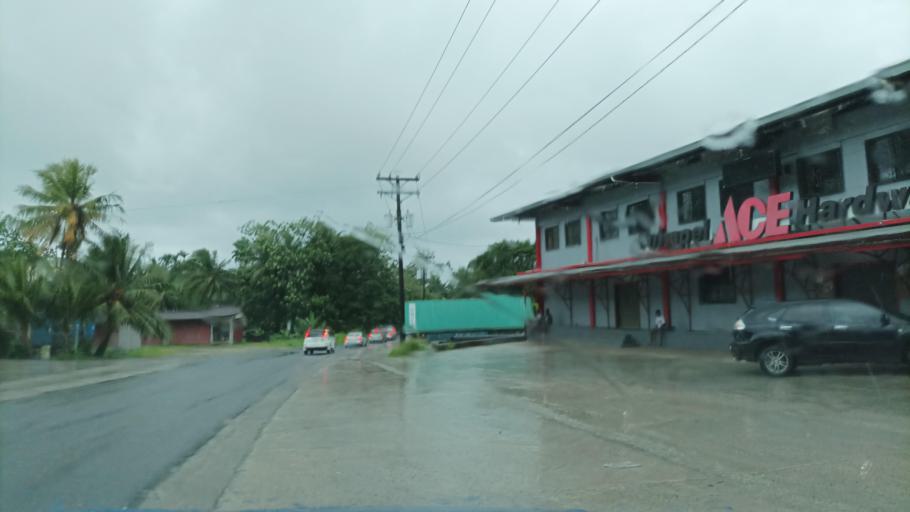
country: FM
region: Pohnpei
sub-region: Kolonia Municipality
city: Kolonia
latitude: 6.9596
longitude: 158.2151
